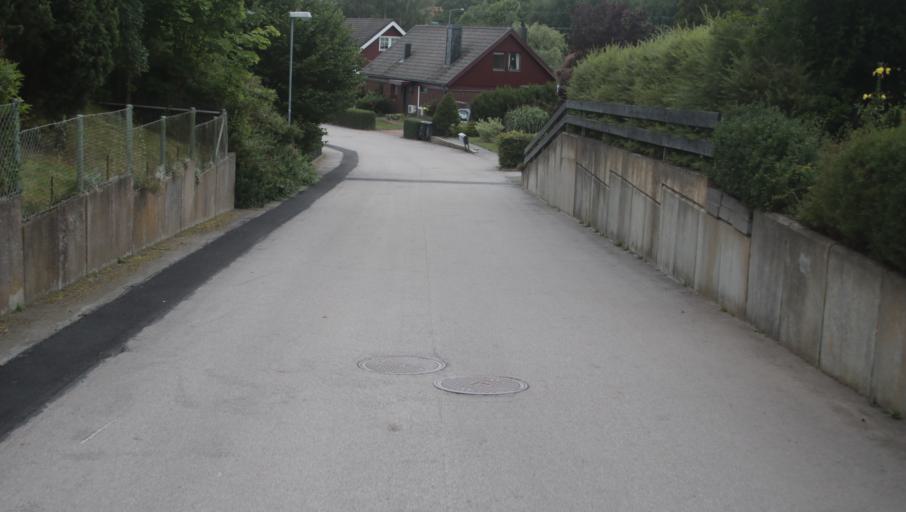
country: SE
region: Blekinge
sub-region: Karlshamns Kommun
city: Morrum
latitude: 56.1953
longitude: 14.7684
